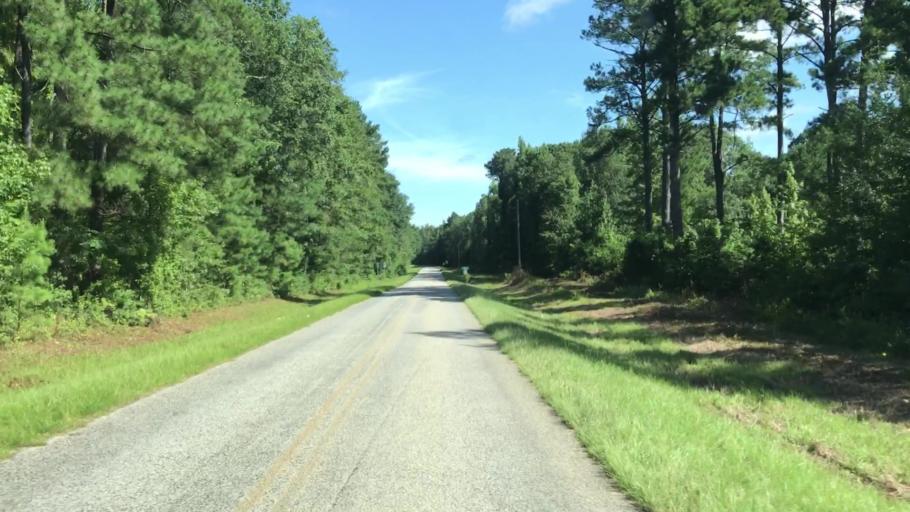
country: US
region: Georgia
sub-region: Jefferson County
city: Wadley
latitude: 32.8140
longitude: -82.3760
